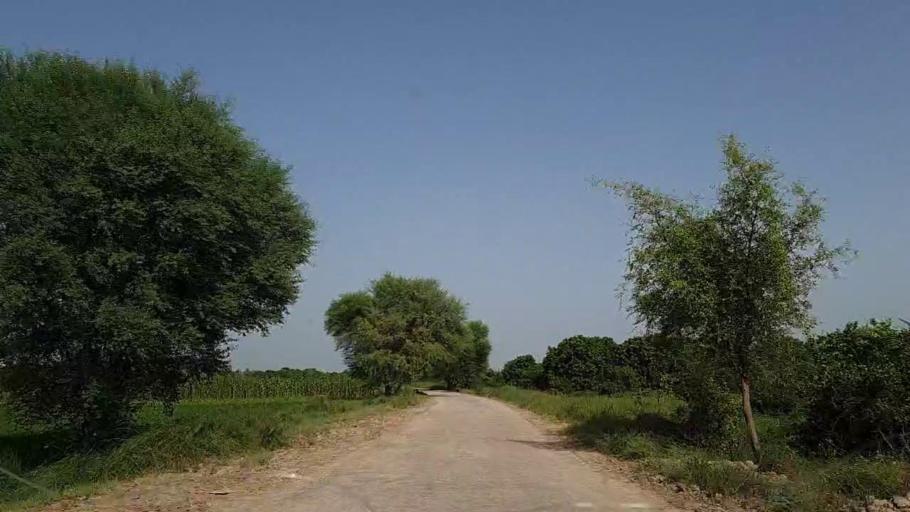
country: PK
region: Sindh
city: Kandiaro
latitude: 27.0682
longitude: 68.1702
